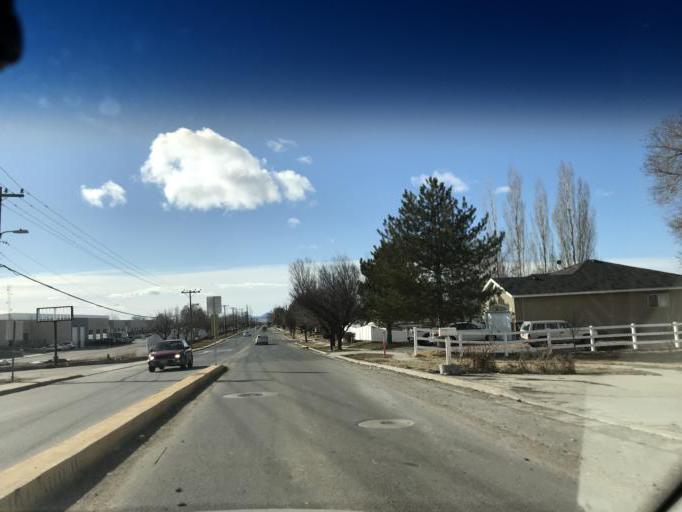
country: US
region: Utah
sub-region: Davis County
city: Woods Cross
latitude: 40.8748
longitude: -111.9059
